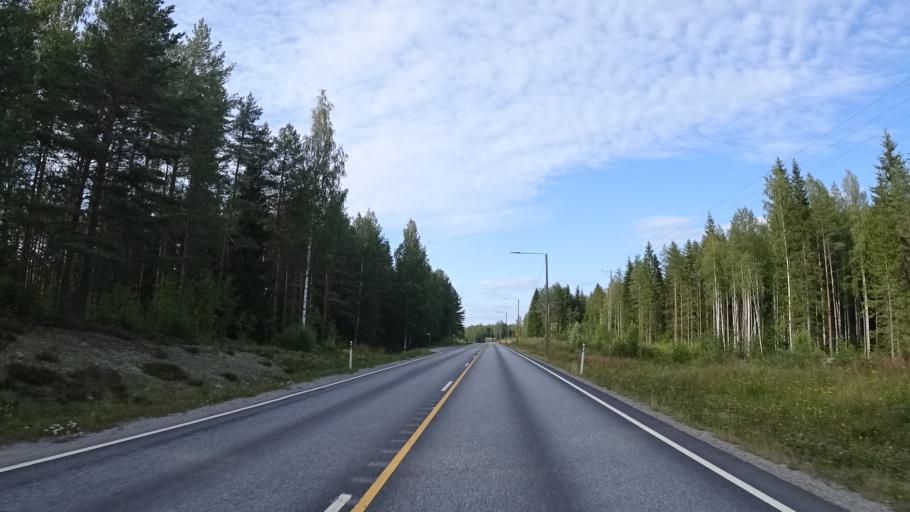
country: FI
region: North Karelia
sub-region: Joensuu
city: Eno
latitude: 62.8607
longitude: 30.1972
